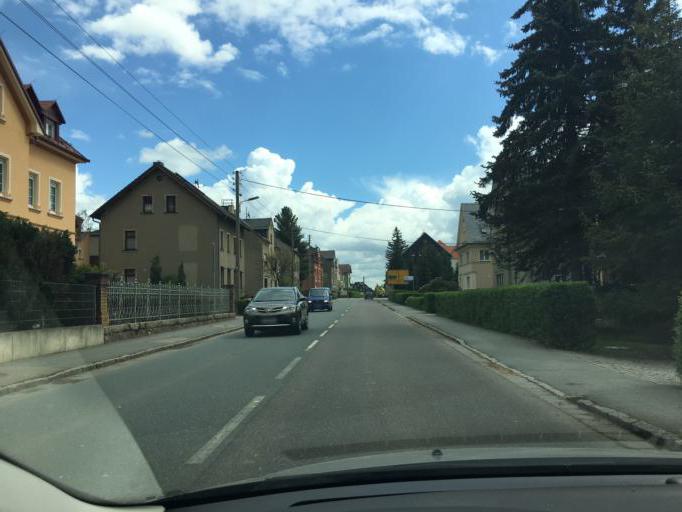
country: DE
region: Saxony
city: Hohenstein-Ernstthal
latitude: 50.8084
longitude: 12.7539
